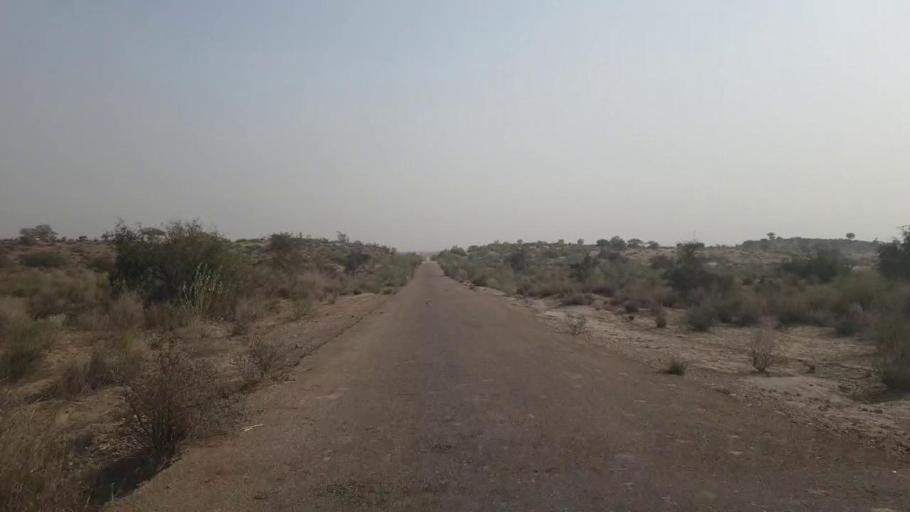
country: PK
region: Sindh
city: Chor
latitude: 25.4453
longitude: 69.9646
